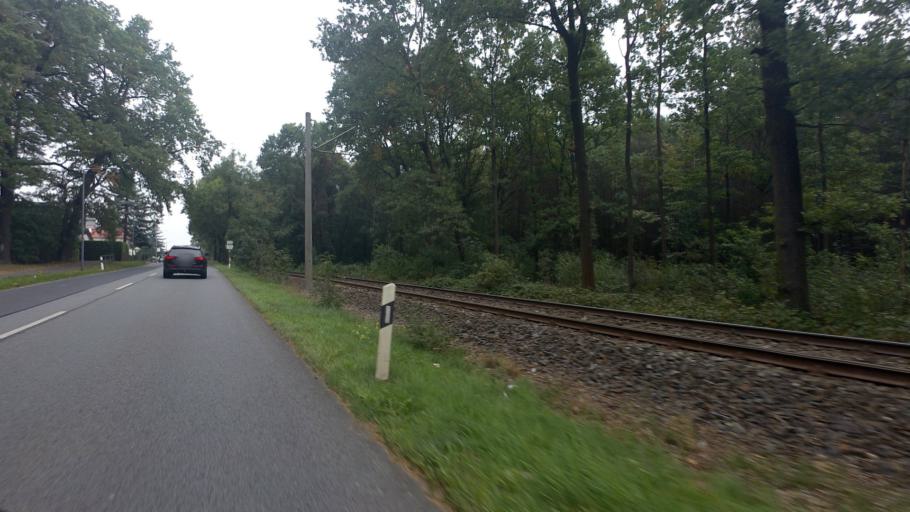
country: DE
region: Saxony
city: Albertstadt
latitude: 51.1317
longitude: 13.7946
